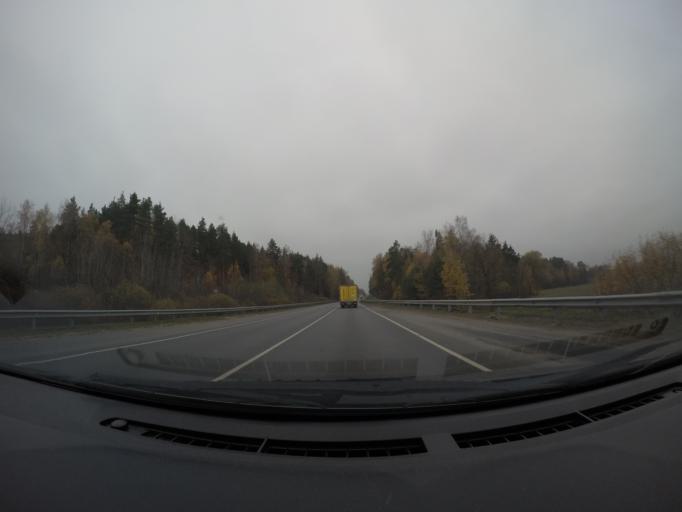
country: RU
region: Moskovskaya
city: Malyshevo
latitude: 55.5302
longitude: 38.3993
